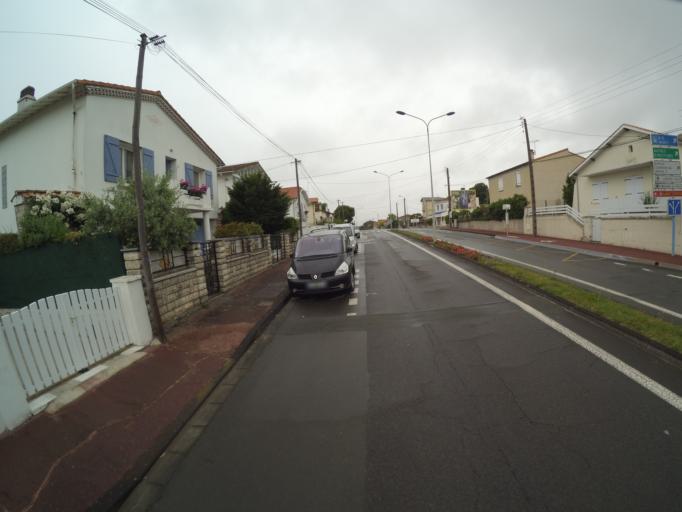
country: FR
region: Poitou-Charentes
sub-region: Departement de la Charente-Maritime
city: Saint-Georges-de-Didonne
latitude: 45.6204
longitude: -1.0080
